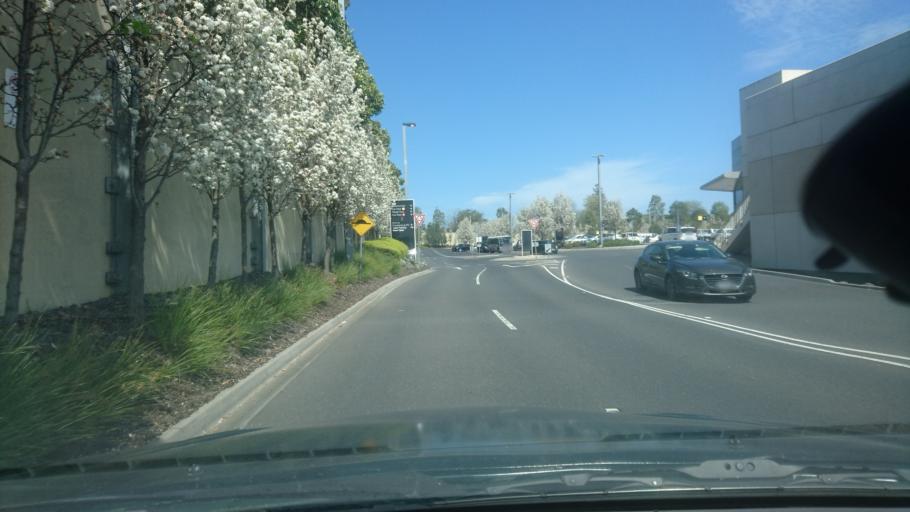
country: AU
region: Victoria
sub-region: Monash
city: Chadstone
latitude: -37.8873
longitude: 145.0861
